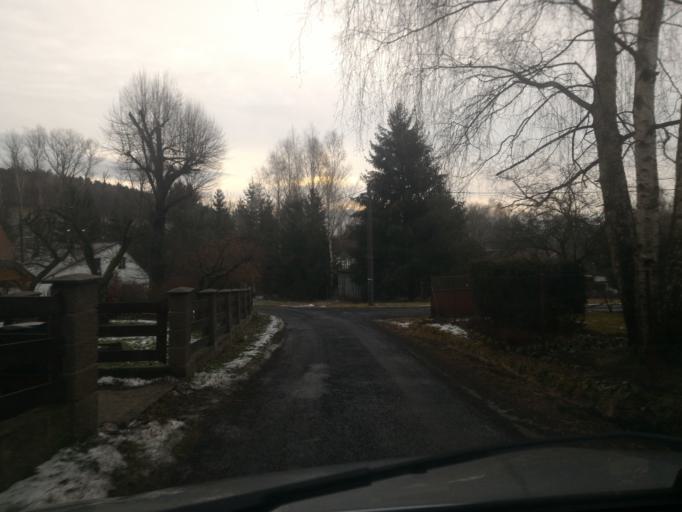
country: DE
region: Saxony
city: Leutersdorf
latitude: 50.9191
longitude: 14.6501
